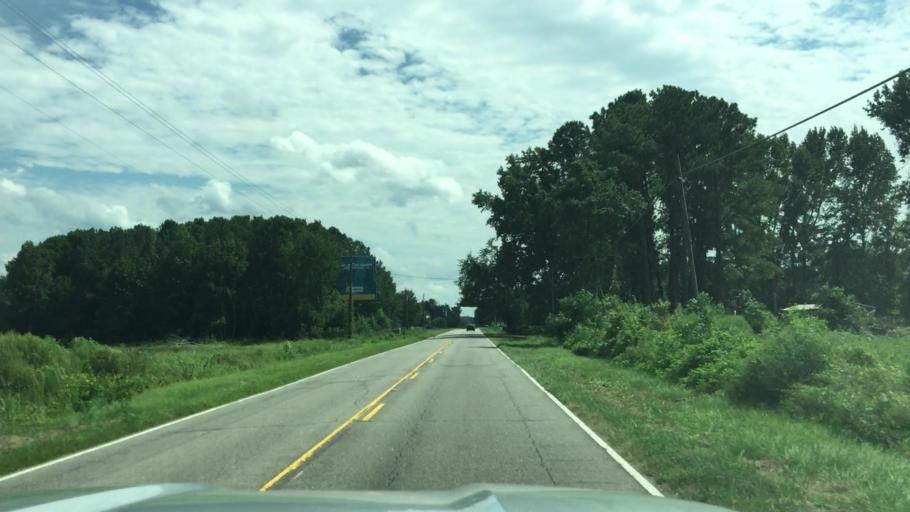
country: US
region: South Carolina
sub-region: Darlington County
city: Hartsville
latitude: 34.3437
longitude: -80.0519
